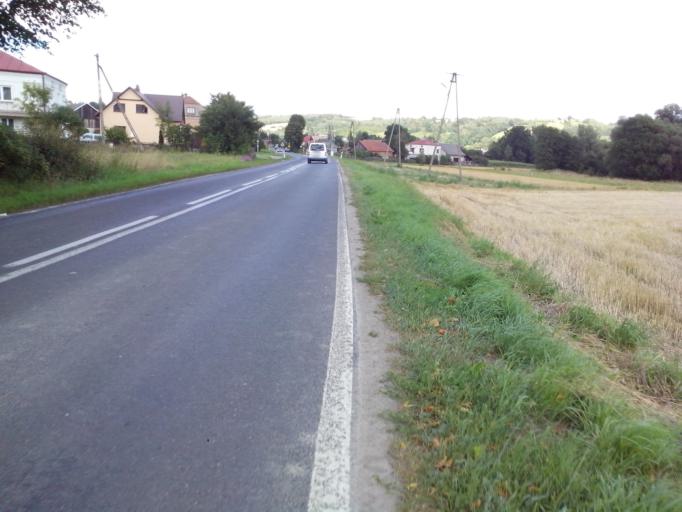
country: PL
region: Subcarpathian Voivodeship
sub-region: Powiat strzyzowski
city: Strzyzow
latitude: 49.8312
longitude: 21.8270
